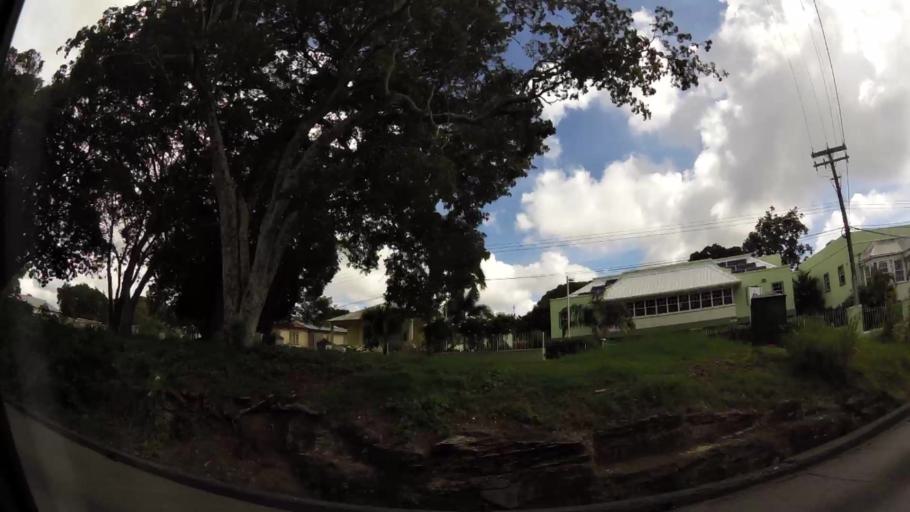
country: BB
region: Saint Michael
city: Bridgetown
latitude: 13.1086
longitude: -59.6164
